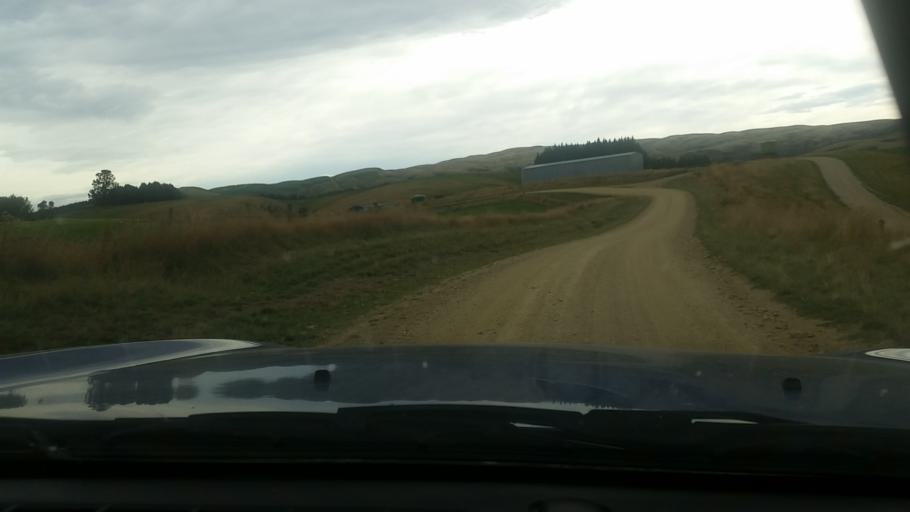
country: NZ
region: Otago
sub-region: Clutha District
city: Balclutha
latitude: -45.6774
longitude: 169.5005
